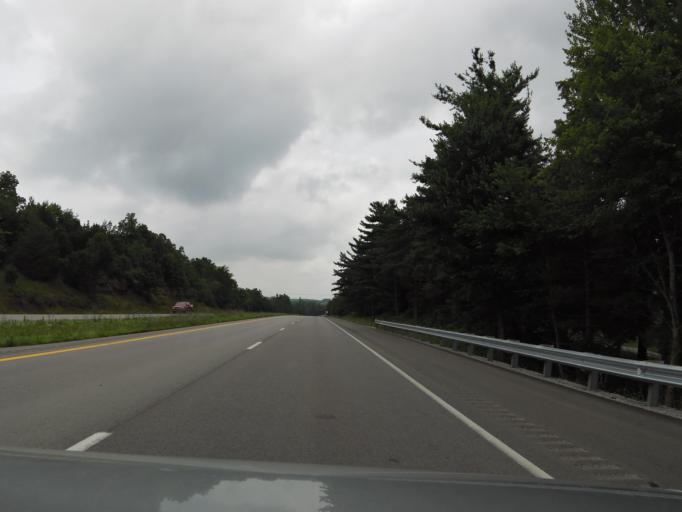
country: US
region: Kentucky
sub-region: Grayson County
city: Leitchfield
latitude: 37.4468
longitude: -86.3449
